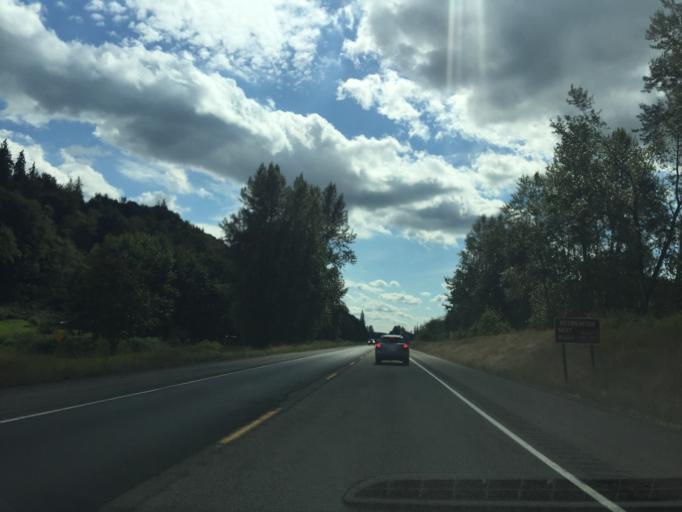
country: US
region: Washington
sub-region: Snohomish County
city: Snohomish
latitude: 47.9289
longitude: -122.0726
